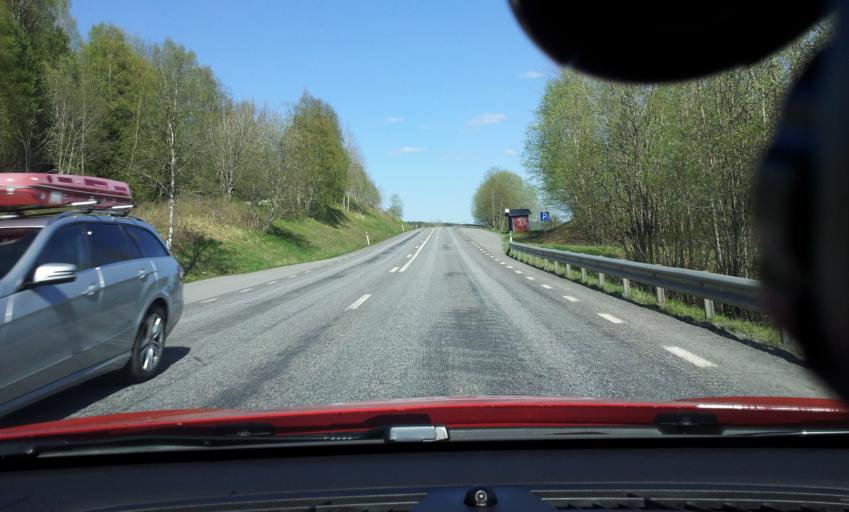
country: SE
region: Jaemtland
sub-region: Are Kommun
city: Jarpen
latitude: 63.3158
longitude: 13.3454
